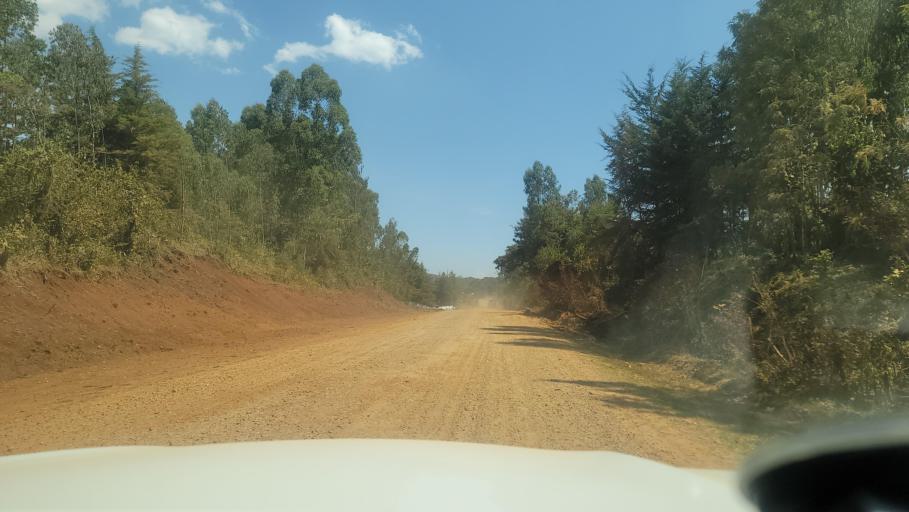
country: ET
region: Oromiya
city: Agaro
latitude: 7.7841
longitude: 36.3493
